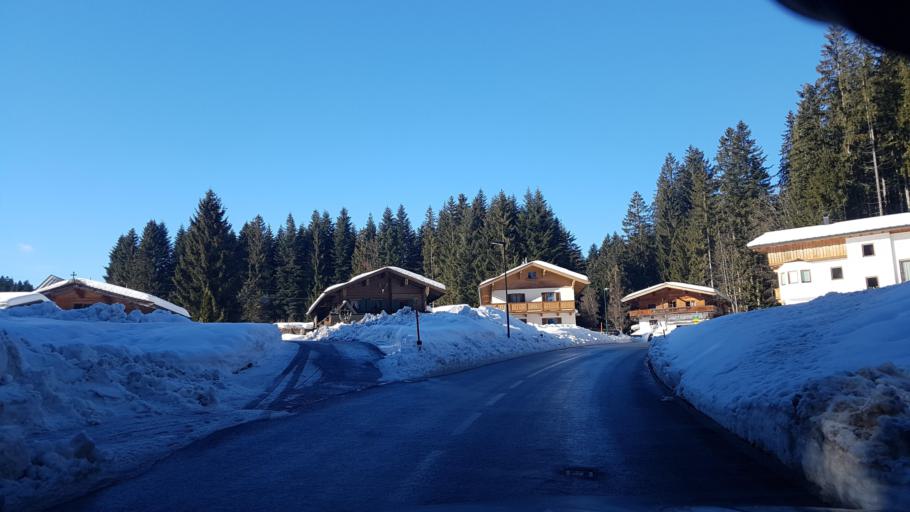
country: AT
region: Tyrol
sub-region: Politischer Bezirk Kitzbuhel
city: Oberndorf in Tirol
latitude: 47.5036
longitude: 12.3757
